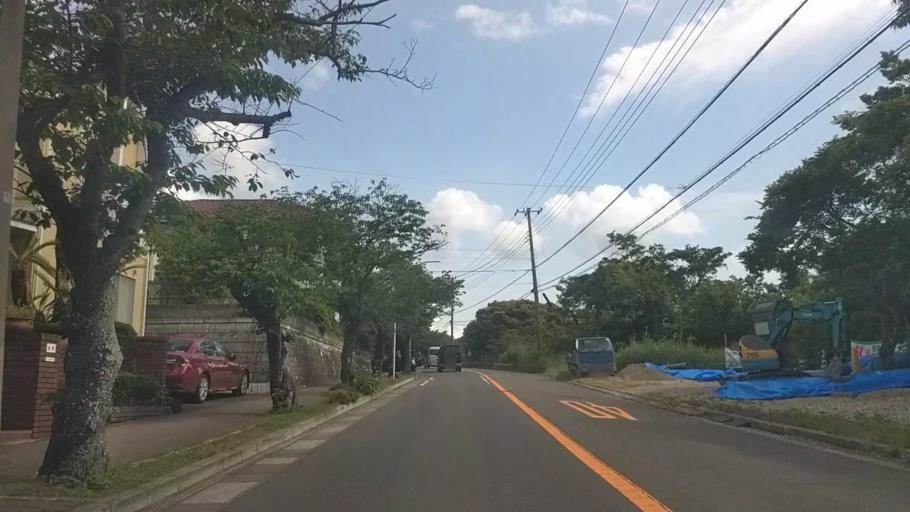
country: JP
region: Kanagawa
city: Zushi
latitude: 35.3100
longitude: 139.5764
